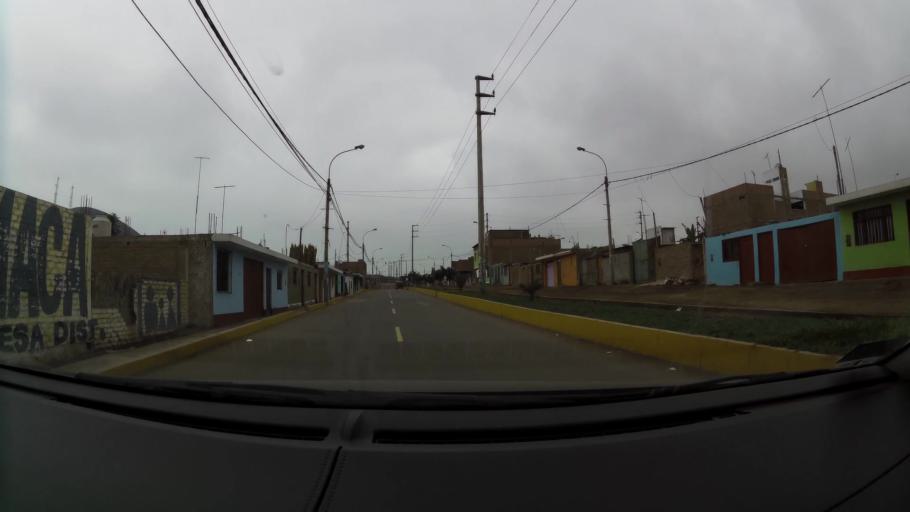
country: PE
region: Lima
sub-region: Provincia de Huaral
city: Chancay
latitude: -11.5859
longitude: -77.2587
